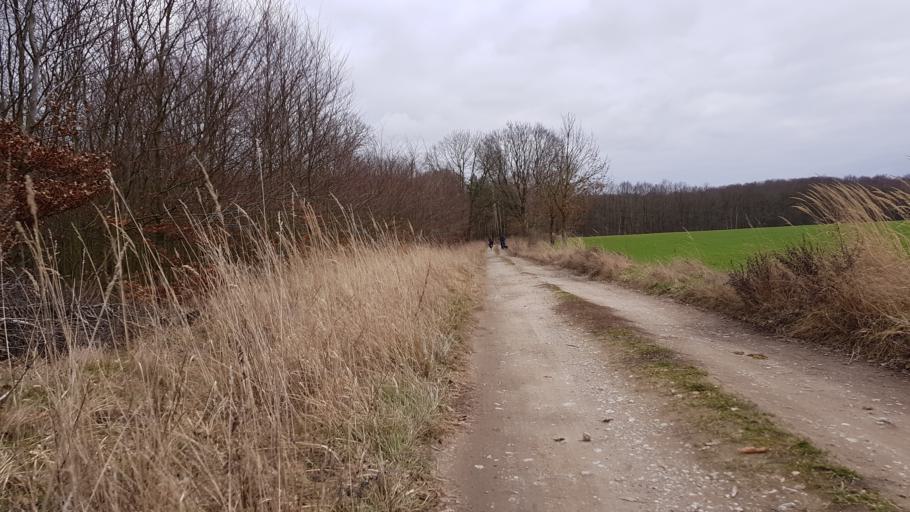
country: PL
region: West Pomeranian Voivodeship
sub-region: Powiat gryfinski
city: Banie
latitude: 53.0743
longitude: 14.7302
